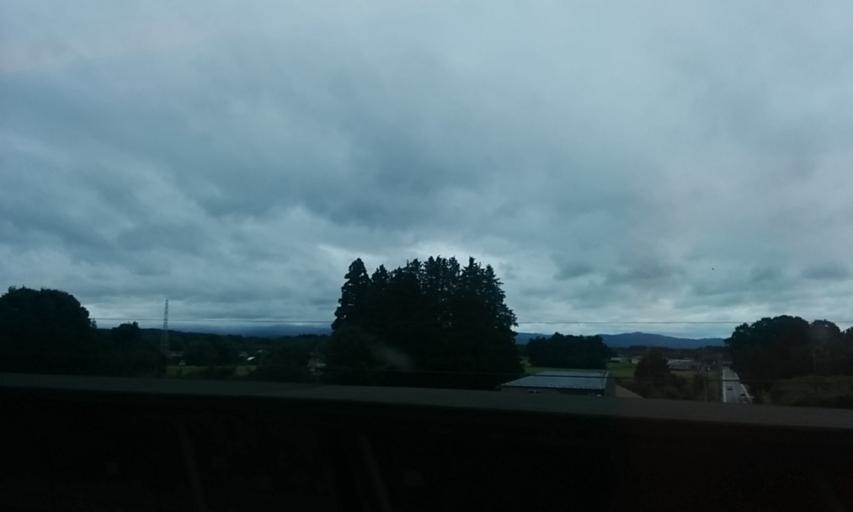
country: JP
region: Tochigi
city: Otawara
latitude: 36.9023
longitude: 139.9992
